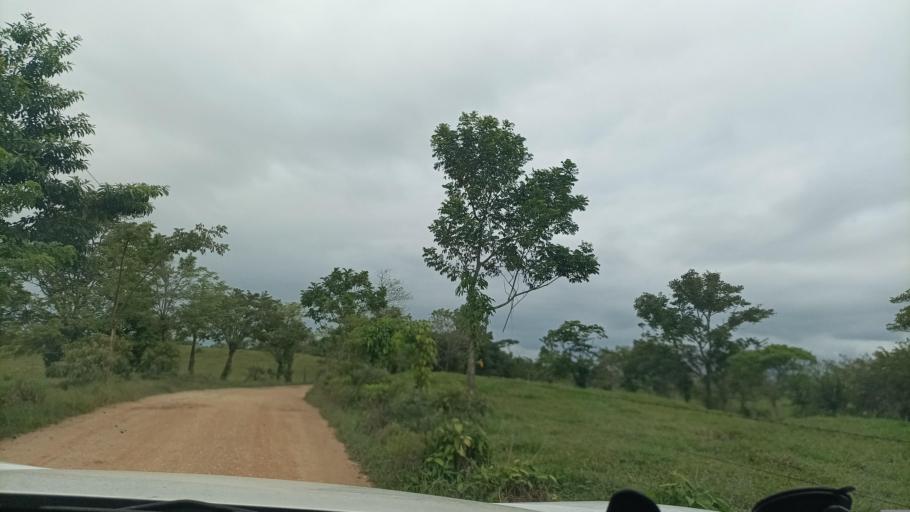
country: MX
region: Veracruz
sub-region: Uxpanapa
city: Poblado Cinco
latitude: 17.4780
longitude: -94.5700
